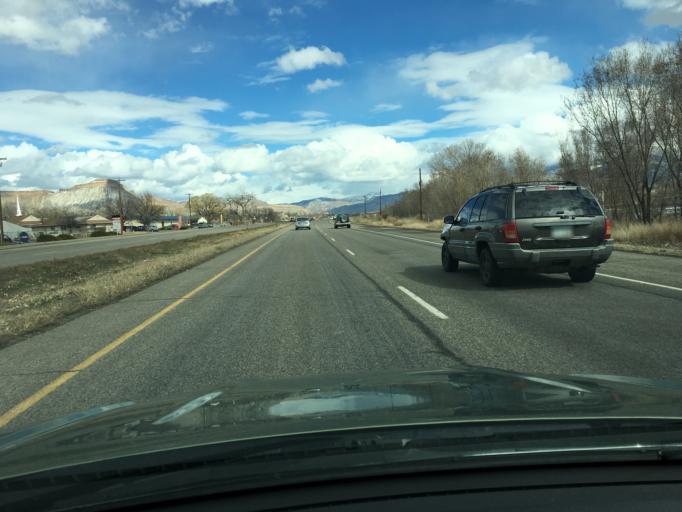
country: US
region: Colorado
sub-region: Mesa County
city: Fruitvale
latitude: 39.0808
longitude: -108.4811
